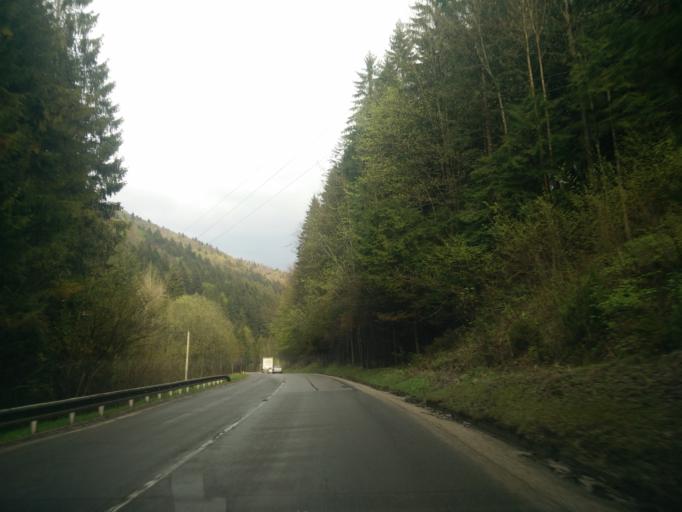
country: SK
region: Banskobystricky
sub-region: Okres Ziar nad Hronom
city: Kremnica
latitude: 48.8451
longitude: 18.9369
